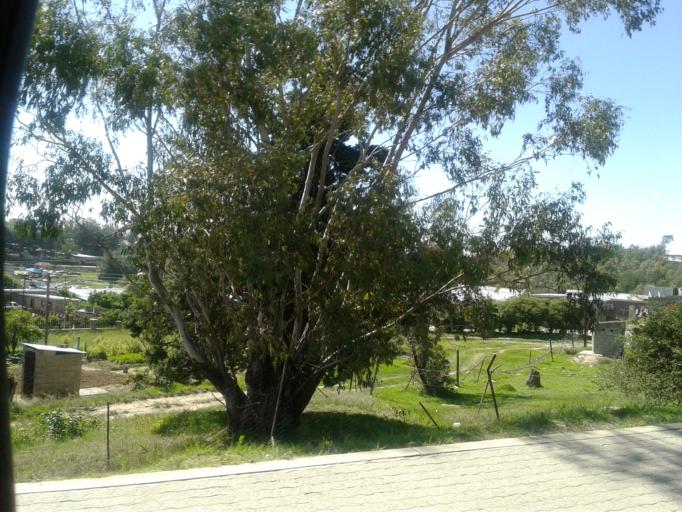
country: LS
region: Butha-Buthe
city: Butha-Buthe
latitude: -28.7651
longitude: 28.2545
